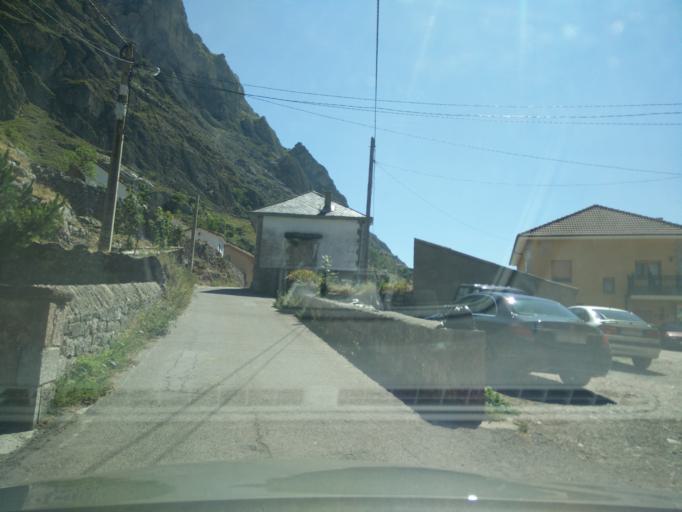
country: ES
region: Asturias
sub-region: Province of Asturias
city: Pola de Somiedo
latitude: 43.0720
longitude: -6.1988
